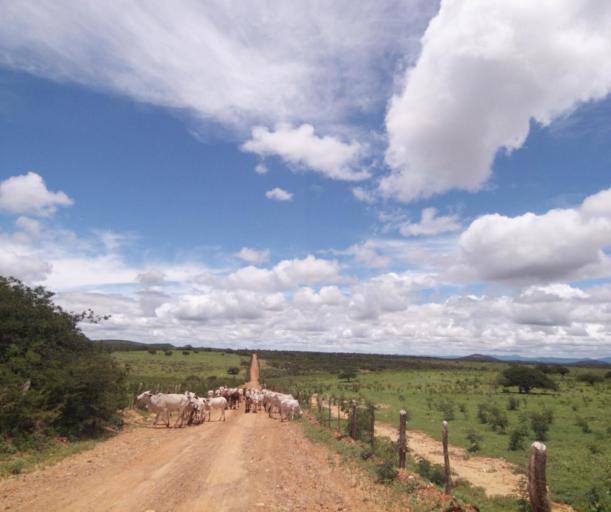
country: BR
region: Bahia
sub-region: Tanhacu
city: Tanhacu
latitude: -14.1914
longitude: -41.0665
